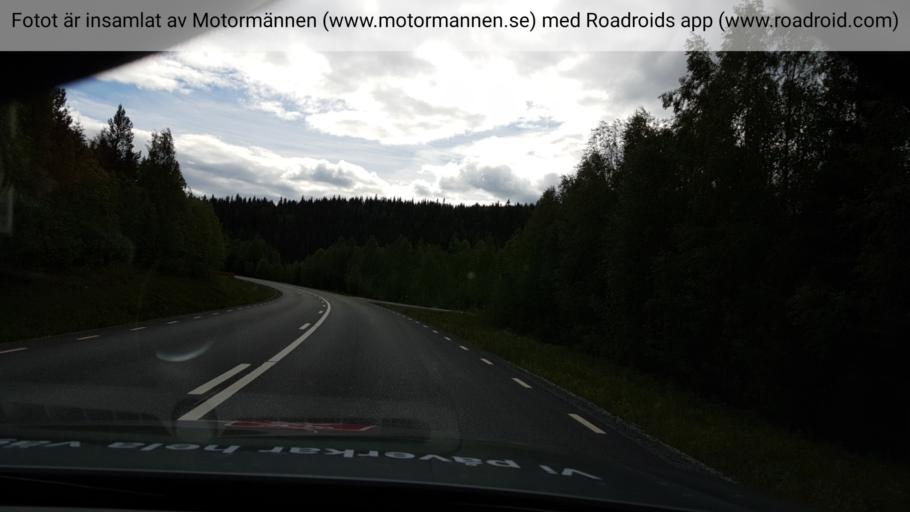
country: SE
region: Jaemtland
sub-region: Stroemsunds Kommun
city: Stroemsund
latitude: 64.1030
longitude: 15.5873
